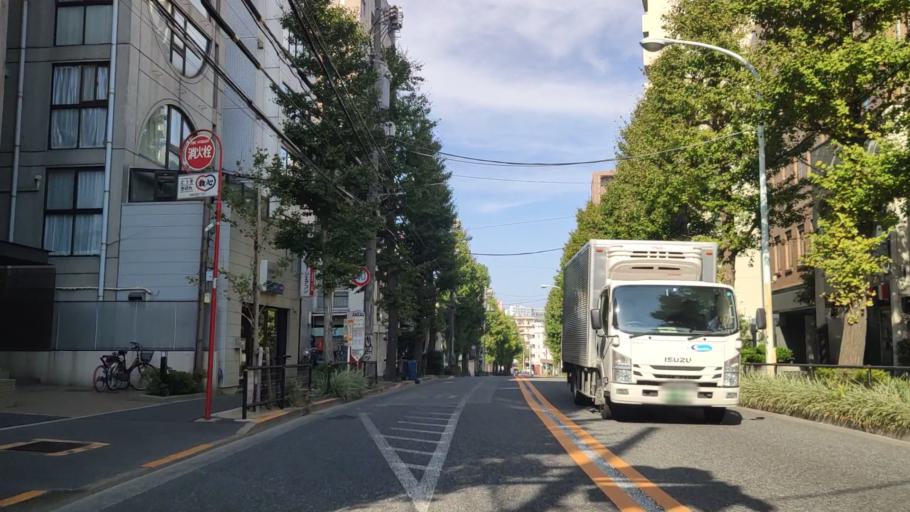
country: JP
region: Tokyo
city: Tokyo
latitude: 35.6889
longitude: 139.6689
